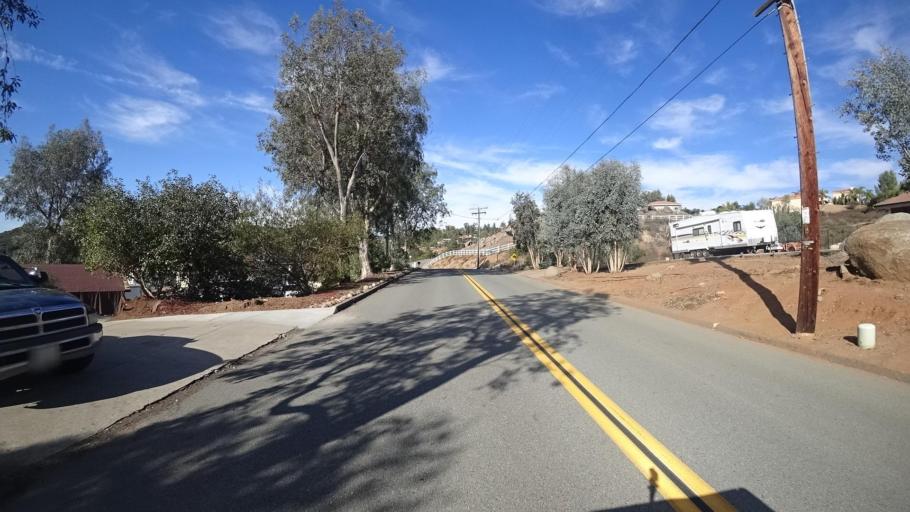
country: US
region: California
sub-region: San Diego County
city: Alpine
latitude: 32.8155
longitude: -116.7397
